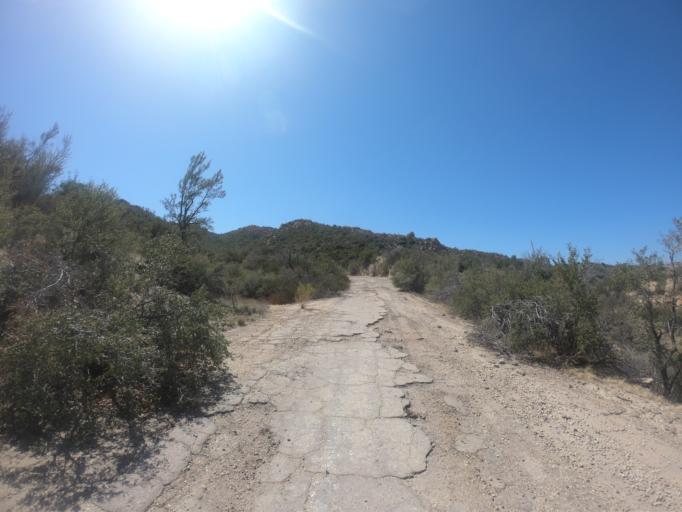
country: US
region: Arizona
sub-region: Gila County
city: Miami
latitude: 33.3585
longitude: -110.9544
